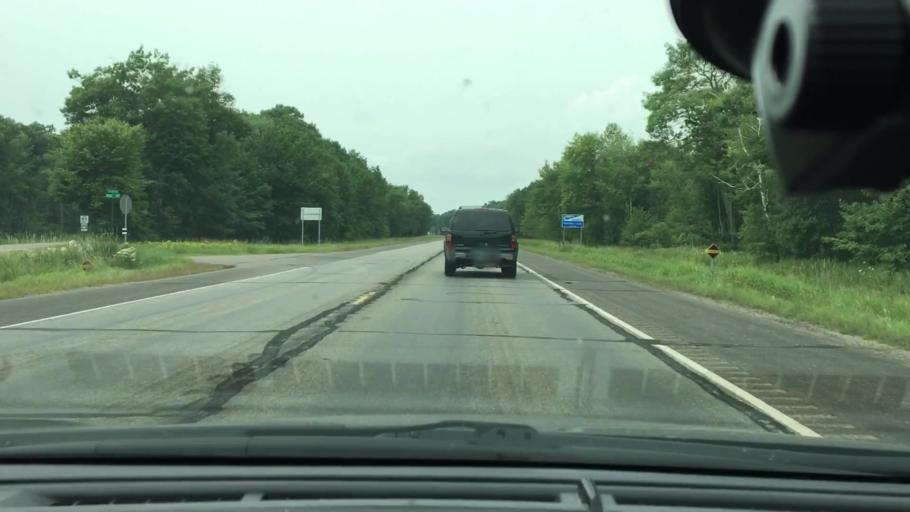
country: US
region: Minnesota
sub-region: Mille Lacs County
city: Vineland
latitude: 46.3253
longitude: -93.7928
